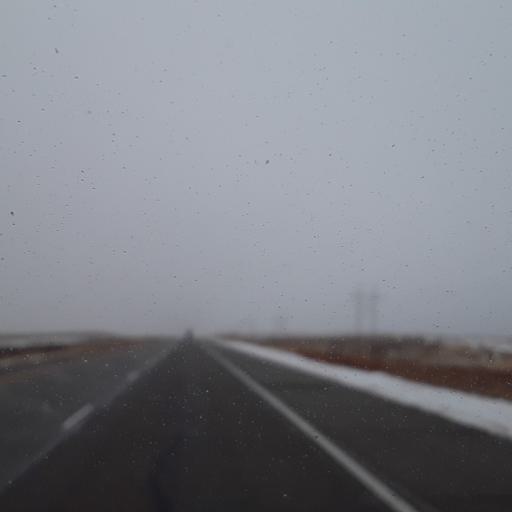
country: US
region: Nebraska
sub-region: Cheyenne County
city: Sidney
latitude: 40.8071
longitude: -102.8515
